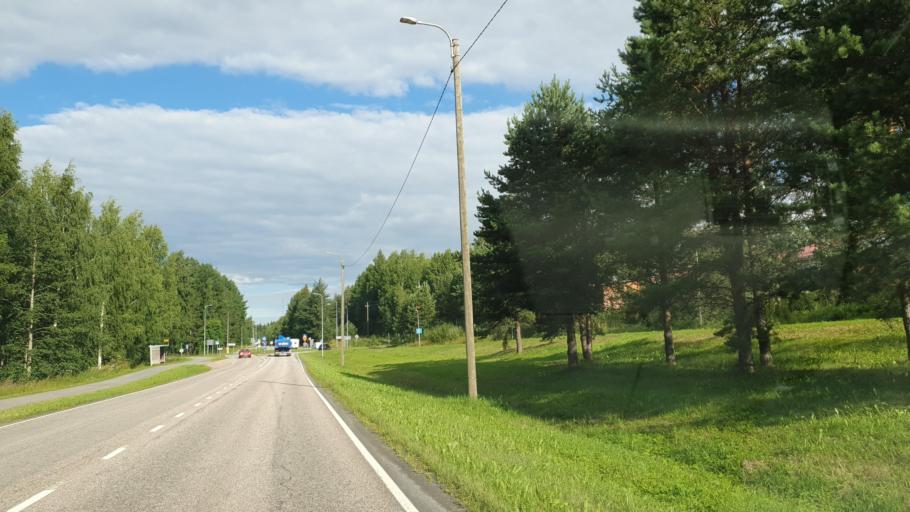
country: FI
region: Central Finland
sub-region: Jyvaeskylae
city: Saeynaetsalo
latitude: 62.1790
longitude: 25.7336
